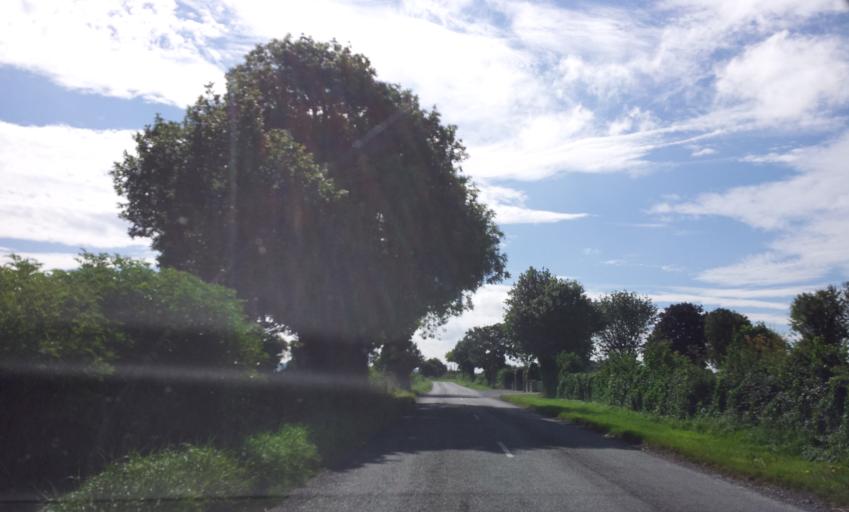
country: IE
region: Leinster
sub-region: Laois
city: Stradbally
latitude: 52.9928
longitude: -7.2207
